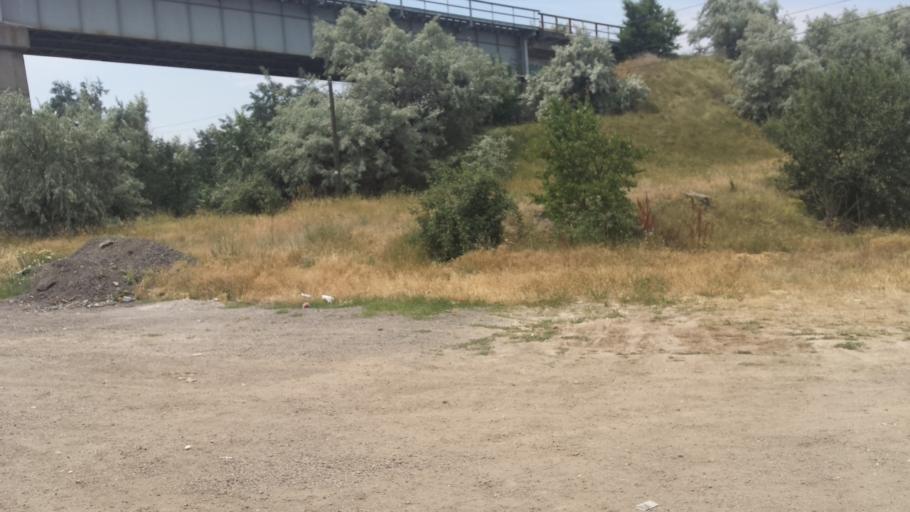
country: RO
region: Constanta
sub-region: Comuna Navodari
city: Navodari
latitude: 44.3269
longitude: 28.6202
